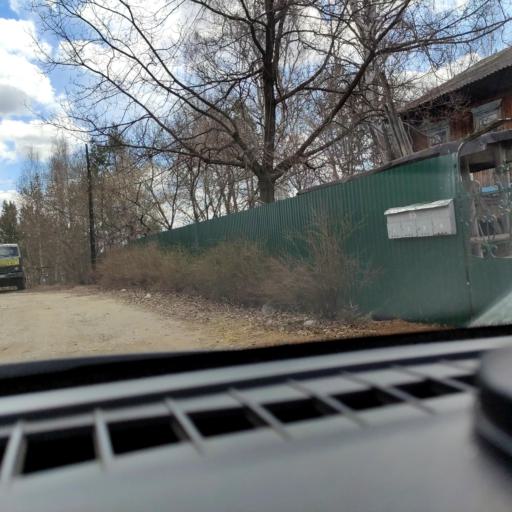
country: RU
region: Perm
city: Perm
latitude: 58.0512
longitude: 56.2968
